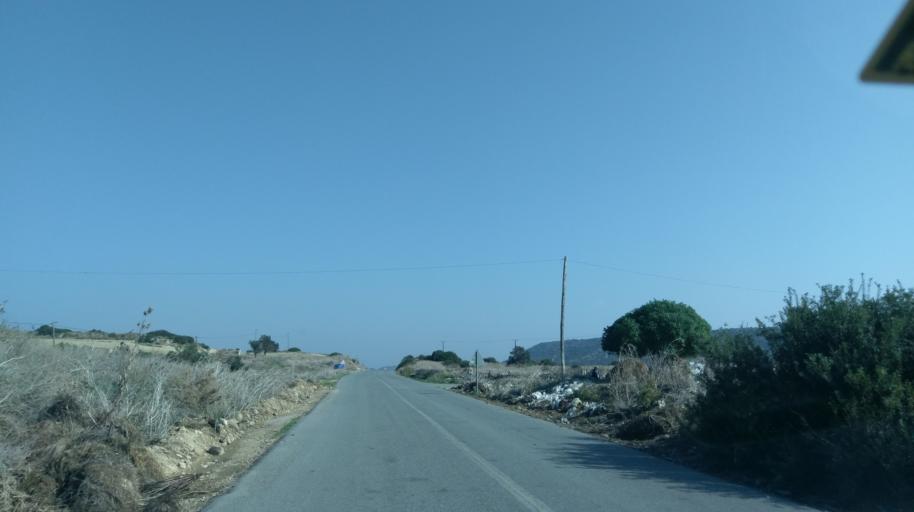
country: CY
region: Ammochostos
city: Leonarisso
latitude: 35.5057
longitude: 34.2484
